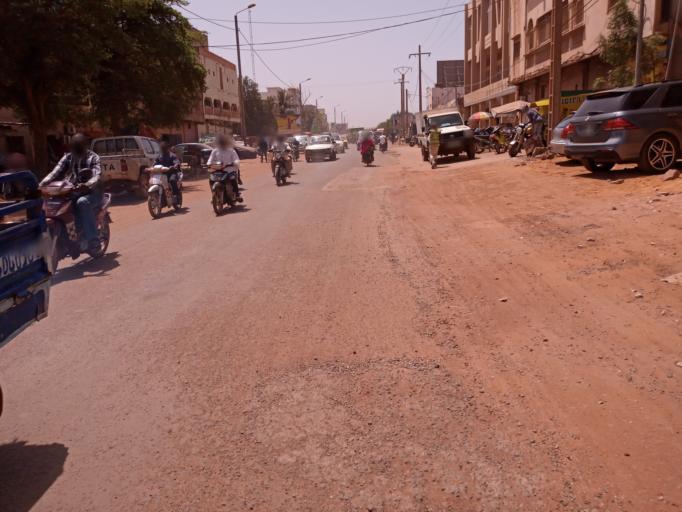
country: ML
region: Bamako
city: Bamako
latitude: 12.6423
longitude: -7.9852
